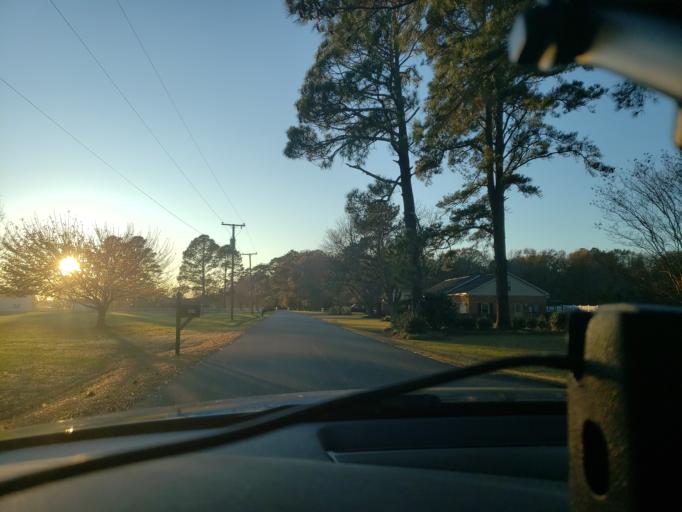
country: US
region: Virginia
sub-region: City of Chesapeake
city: Chesapeake
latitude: 36.7048
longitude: -76.1553
